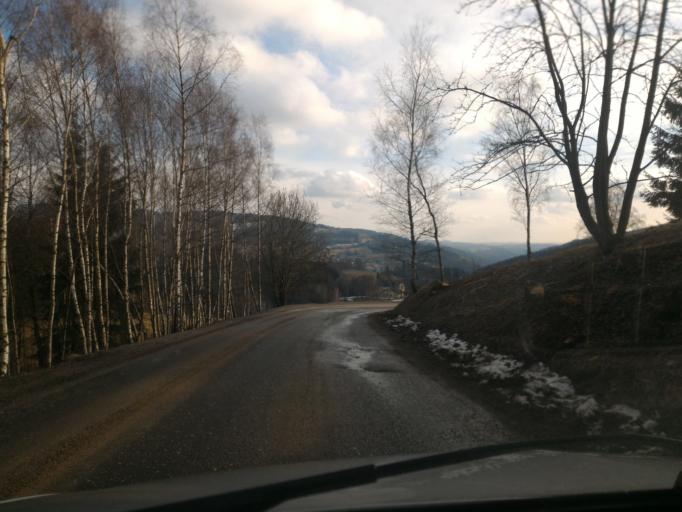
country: CZ
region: Liberecky
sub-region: Okres Jablonec nad Nisou
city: Desna
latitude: 50.7561
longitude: 15.2988
